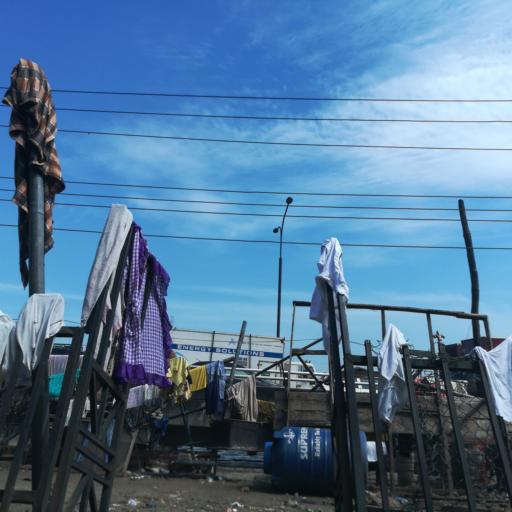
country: NG
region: Lagos
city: Lagos
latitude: 6.4651
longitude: 3.3879
